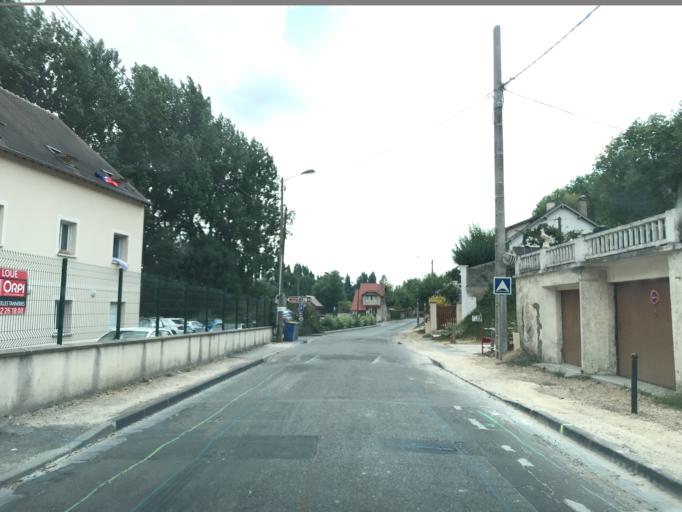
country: FR
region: Haute-Normandie
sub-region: Departement de l'Eure
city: Ivry-la-Bataille
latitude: 48.8774
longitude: 1.4578
